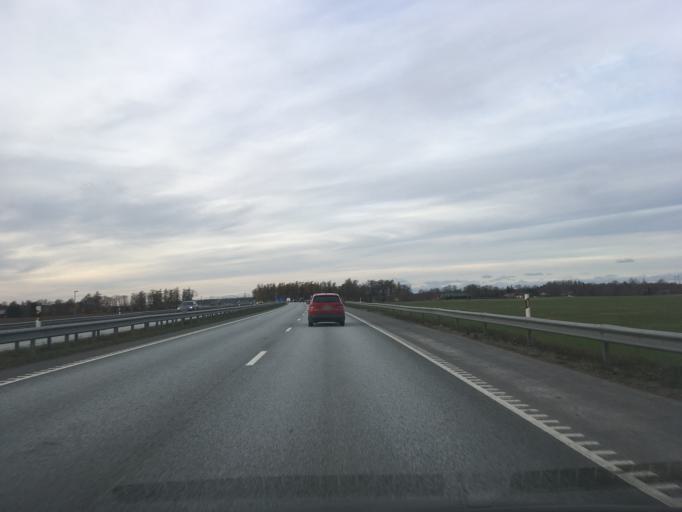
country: EE
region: Ida-Virumaa
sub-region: Johvi vald
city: Johvi
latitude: 59.3803
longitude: 27.3706
